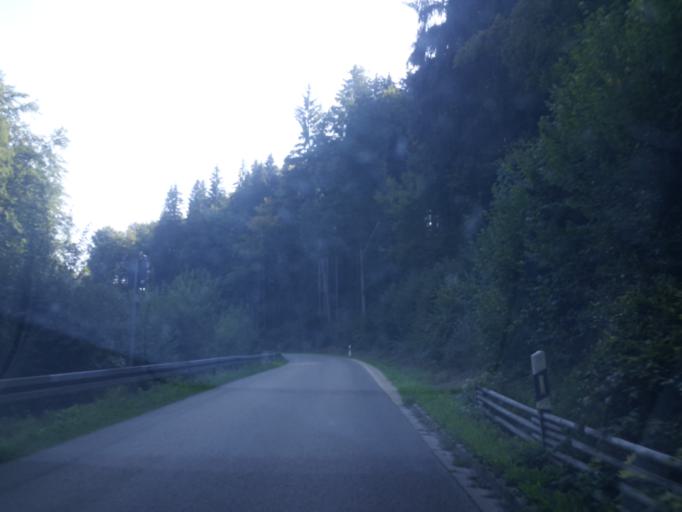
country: DE
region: Bavaria
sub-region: Upper Bavaria
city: Denkendorf
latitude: 48.9239
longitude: 11.4059
